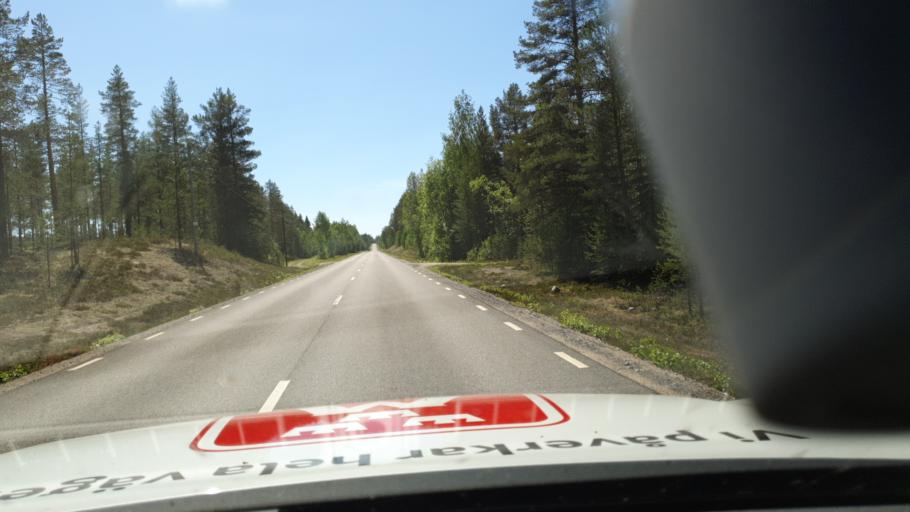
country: SE
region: Jaemtland
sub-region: Harjedalens Kommun
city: Sveg
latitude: 62.1440
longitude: 13.8344
